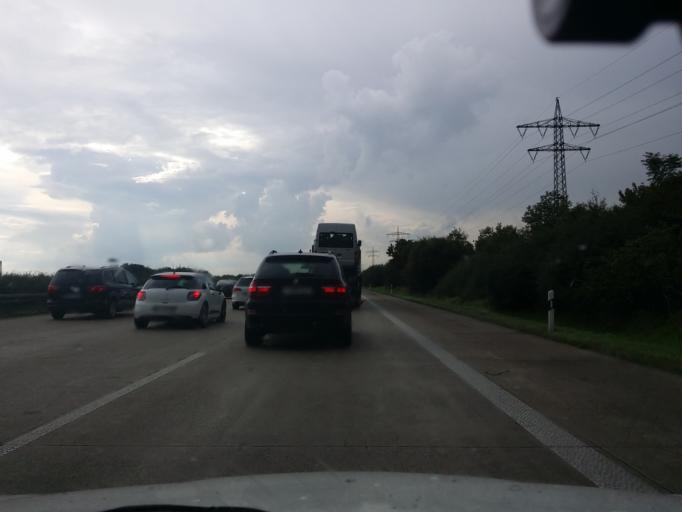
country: DE
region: Thuringia
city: Gosen
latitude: 50.9797
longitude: 11.8765
